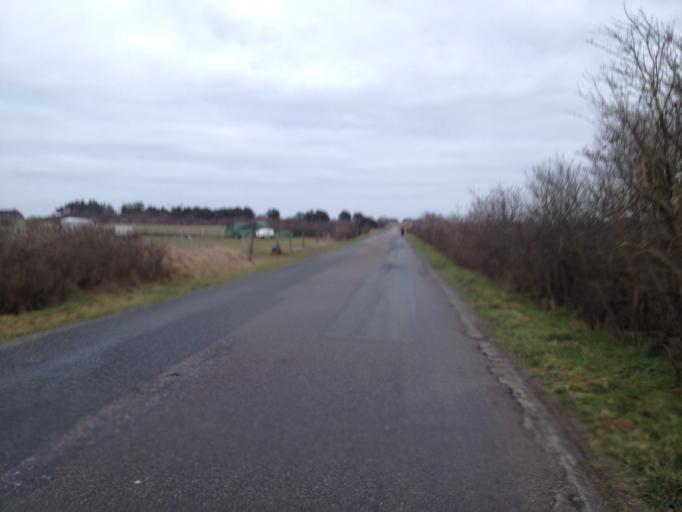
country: DE
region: Schleswig-Holstein
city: Nebel
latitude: 54.6463
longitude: 8.3475
